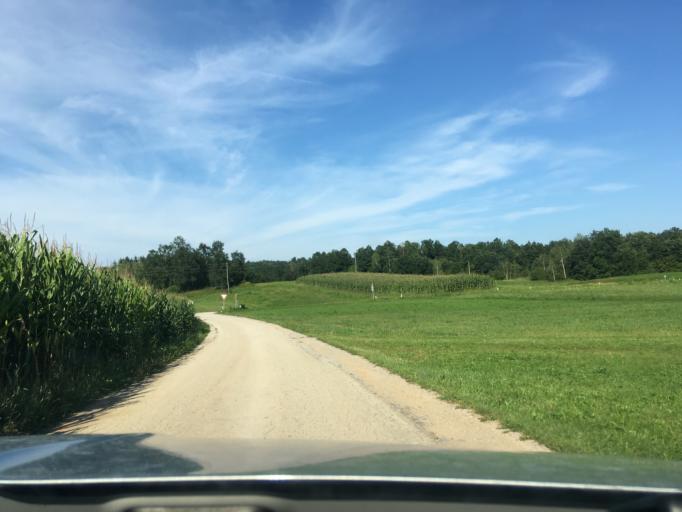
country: SI
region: Crnomelj
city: Crnomelj
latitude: 45.4772
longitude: 15.2090
